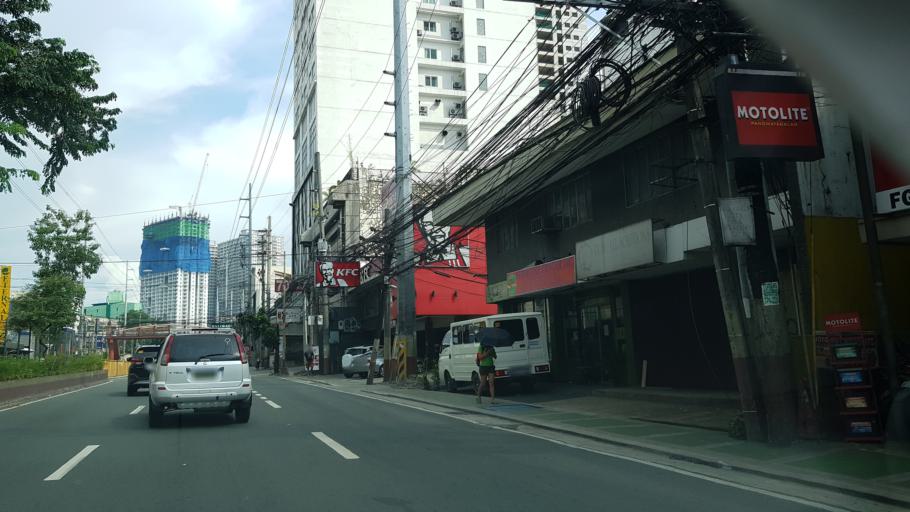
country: PH
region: Metro Manila
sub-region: Pasig
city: Pasig City
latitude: 14.5736
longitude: 121.0625
